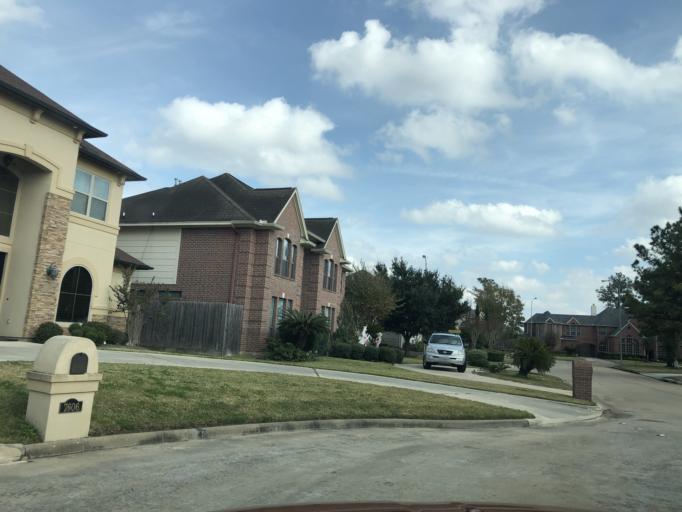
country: US
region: Texas
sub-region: Harris County
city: Tomball
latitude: 30.0358
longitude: -95.5400
